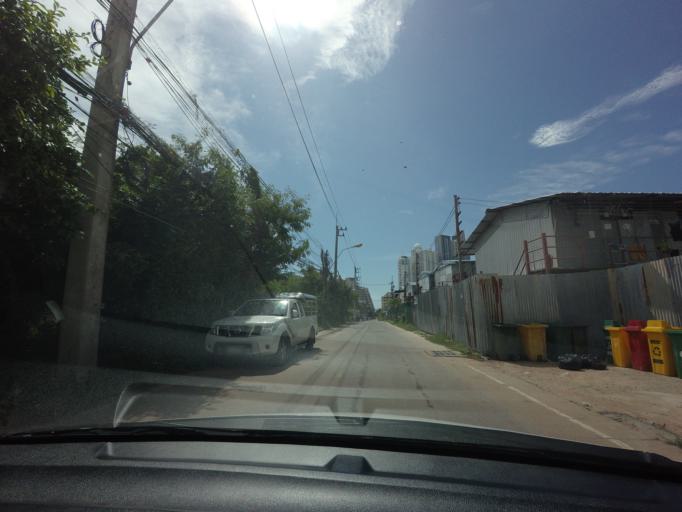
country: TH
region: Chon Buri
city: Phatthaya
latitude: 12.9578
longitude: 100.8908
